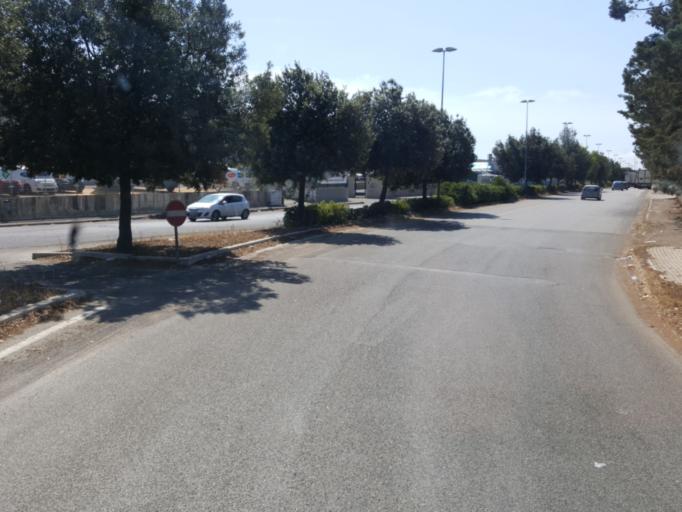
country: IT
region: Latium
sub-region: Citta metropolitana di Roma Capitale
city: Aurelia
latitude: 42.1199
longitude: 11.7783
